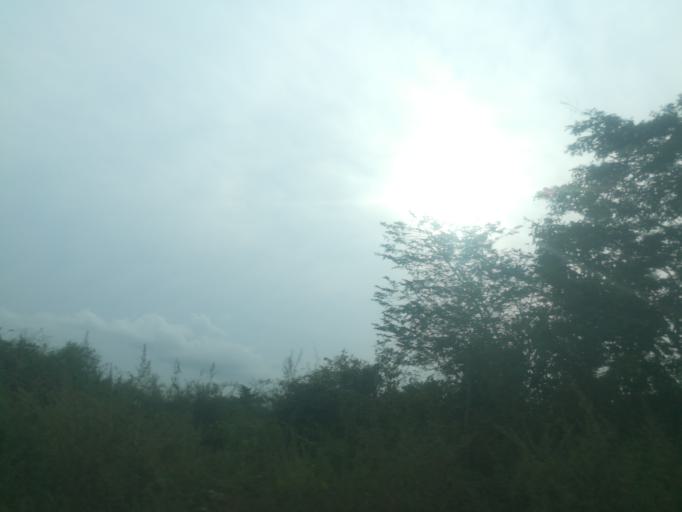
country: NG
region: Ogun
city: Ayetoro
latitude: 7.2452
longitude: 3.1220
